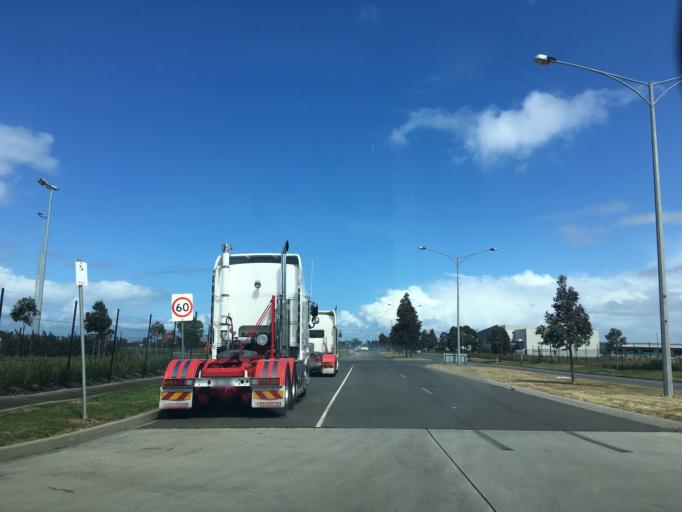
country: AU
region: Victoria
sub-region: Hobsons Bay
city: Altona
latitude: -37.8405
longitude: 144.8105
